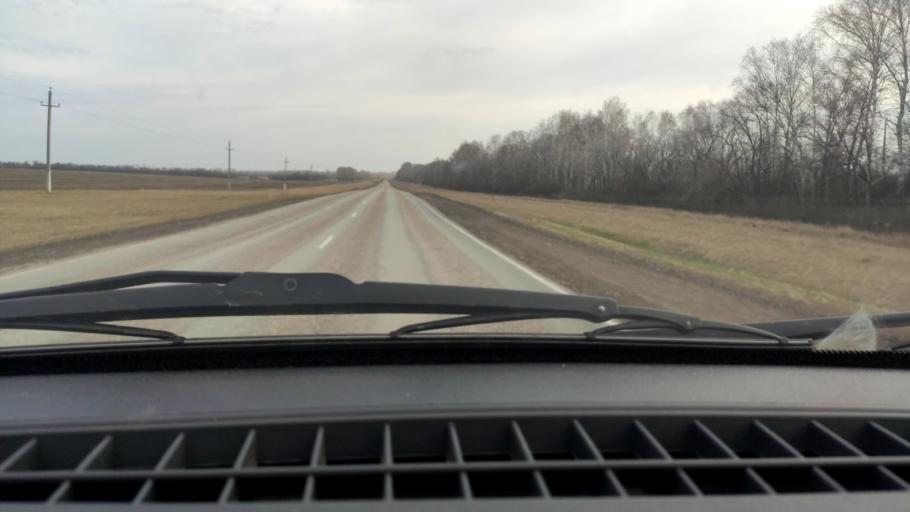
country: RU
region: Bashkortostan
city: Davlekanovo
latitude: 54.3328
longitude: 55.1672
